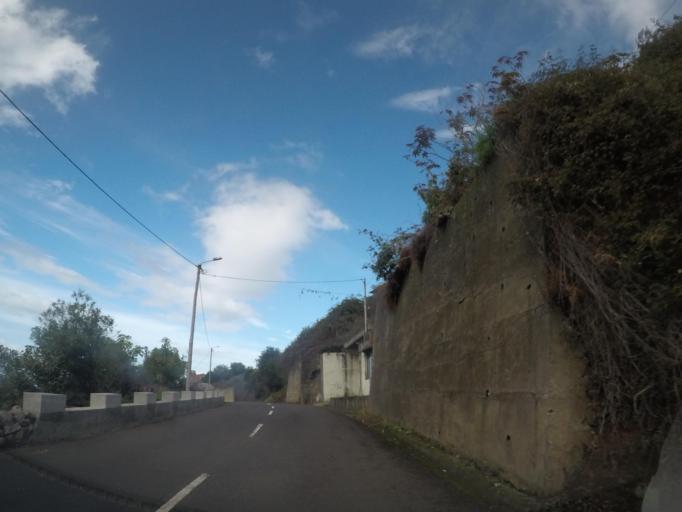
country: PT
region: Madeira
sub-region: Santana
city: Santana
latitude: 32.7881
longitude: -16.8484
